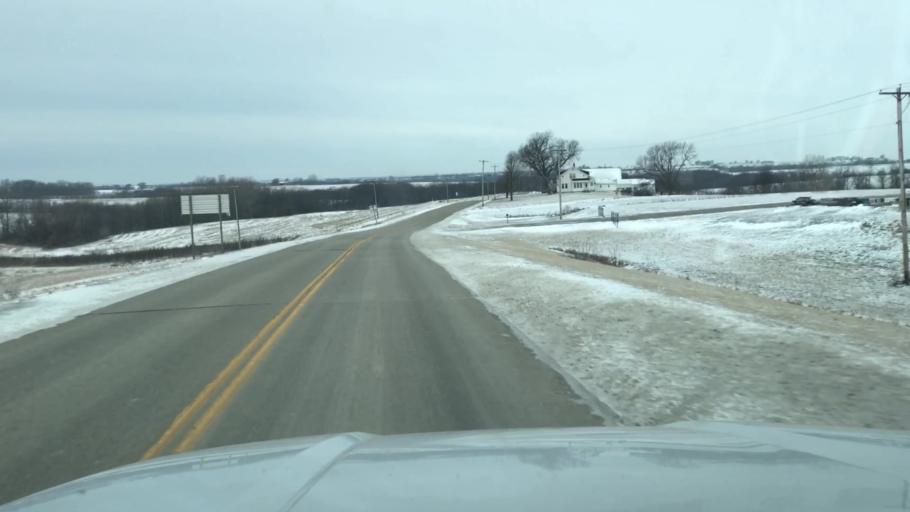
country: US
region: Missouri
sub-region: Andrew County
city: Savannah
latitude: 40.0257
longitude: -94.8812
